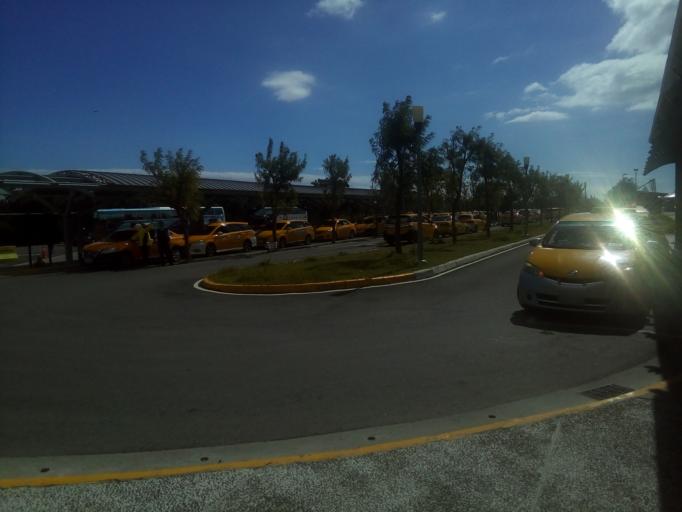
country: TW
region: Taiwan
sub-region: Taitung
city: Taitung
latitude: 22.7928
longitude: 121.1231
